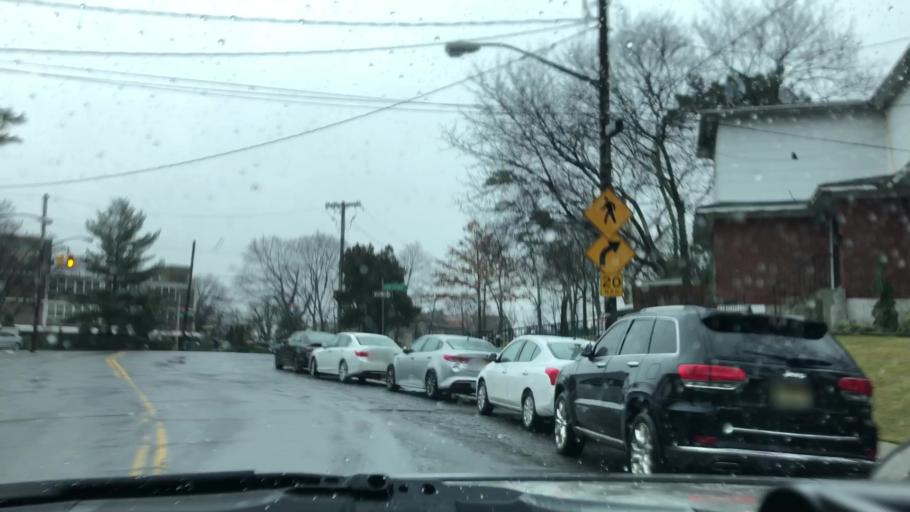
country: US
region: New Jersey
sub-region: Hudson County
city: Bayonne
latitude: 40.6331
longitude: -74.0931
